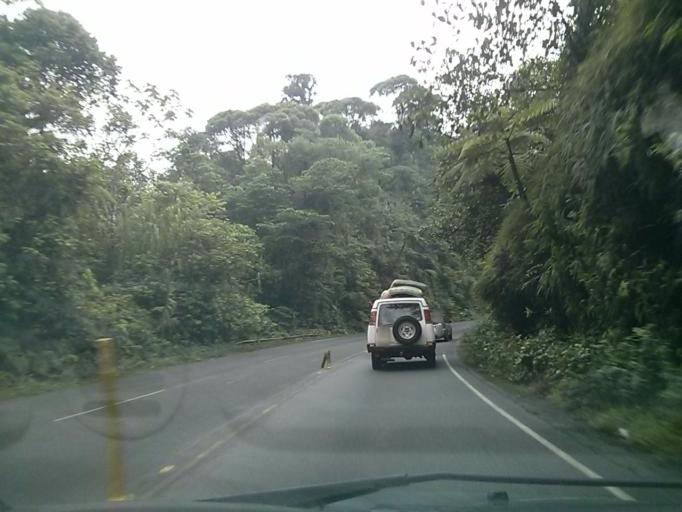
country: CR
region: San Jose
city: Dulce Nombre de Jesus
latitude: 10.1503
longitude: -83.9729
